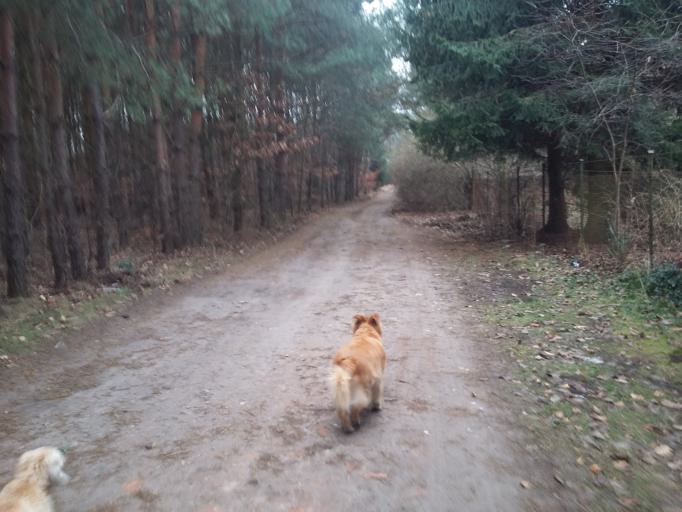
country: PL
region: Lodz Voivodeship
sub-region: Powiat pabianicki
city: Ksawerow
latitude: 51.7273
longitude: 19.3832
